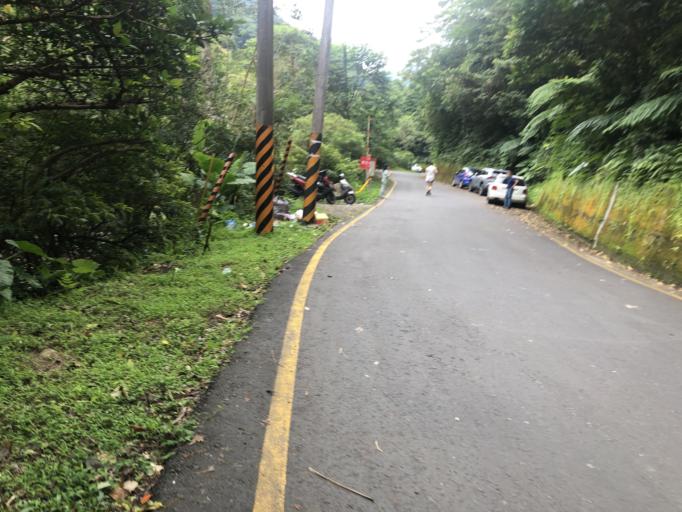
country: TW
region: Taipei
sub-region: Taipei
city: Banqiao
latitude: 24.8462
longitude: 121.4547
